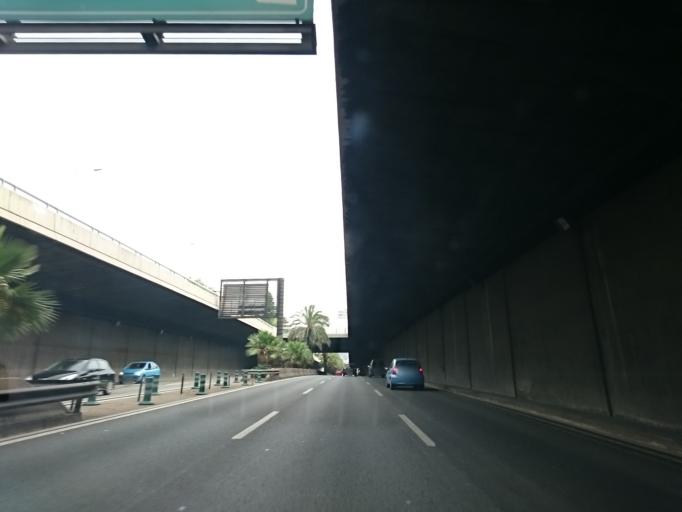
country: ES
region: Catalonia
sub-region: Provincia de Barcelona
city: Sarria-Sant Gervasi
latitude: 41.4210
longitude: 2.1405
